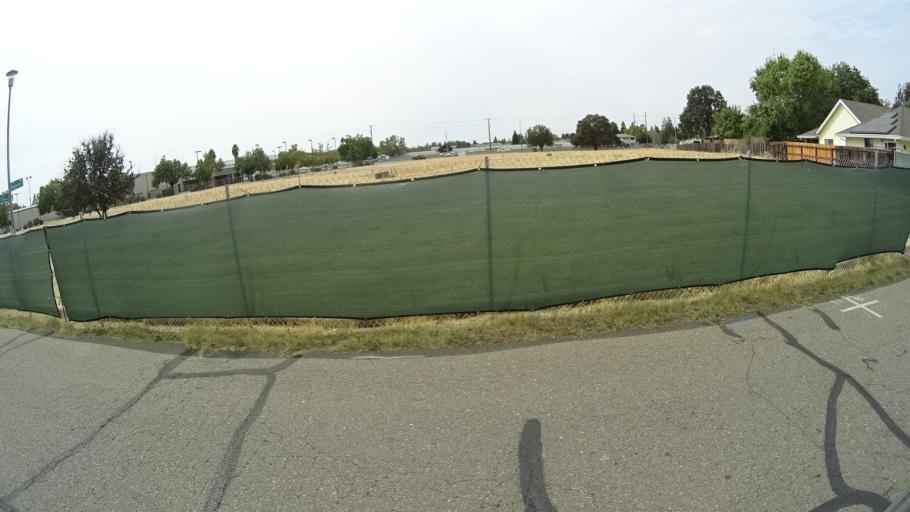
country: US
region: California
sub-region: Sacramento County
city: Elk Grove
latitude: 38.4145
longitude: -121.3888
